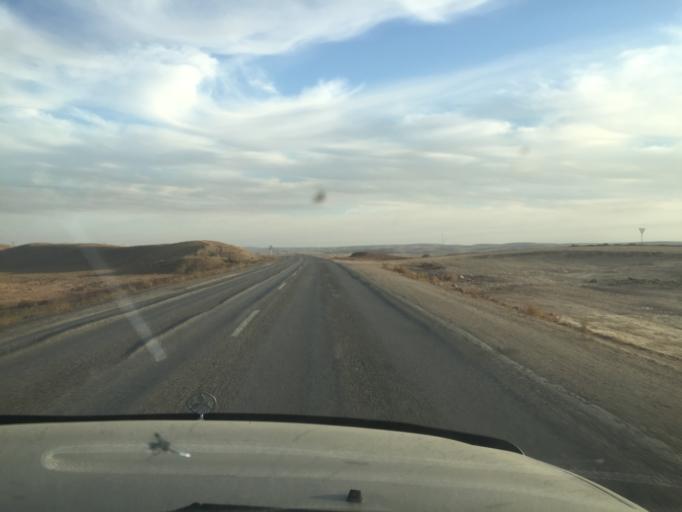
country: KZ
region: Almaty Oblysy
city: Ulken
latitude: 45.0797
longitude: 73.9731
